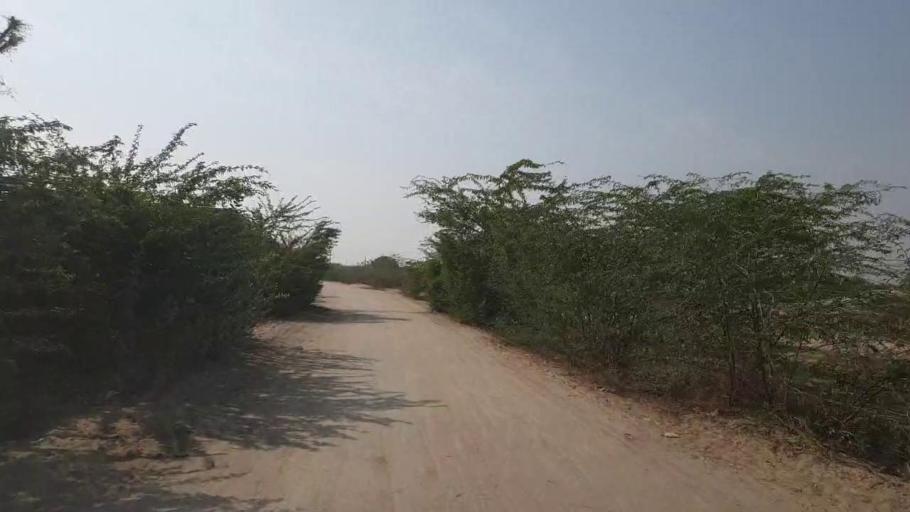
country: PK
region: Sindh
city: Umarkot
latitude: 25.3335
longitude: 69.7349
